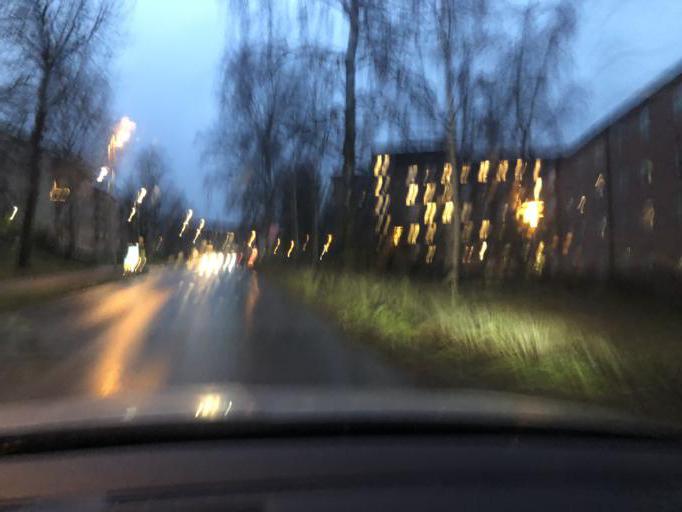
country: SE
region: Vaermland
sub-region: Karlstads Kommun
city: Karlstad
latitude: 59.3765
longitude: 13.4821
